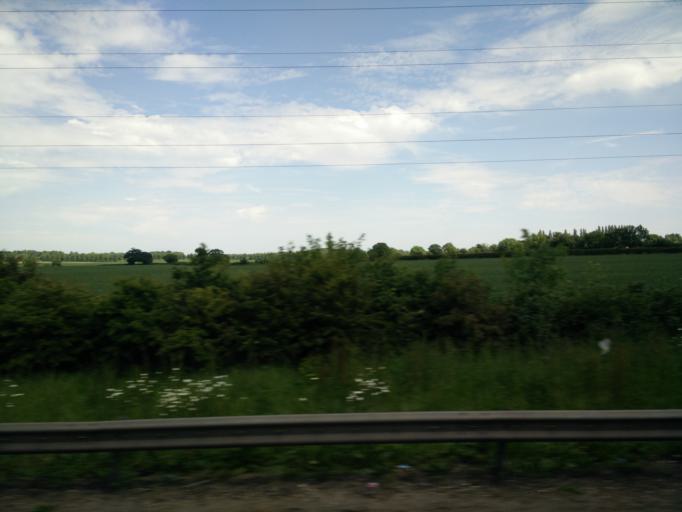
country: GB
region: England
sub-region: Hertfordshire
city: Flamstead
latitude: 51.8375
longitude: -0.4198
